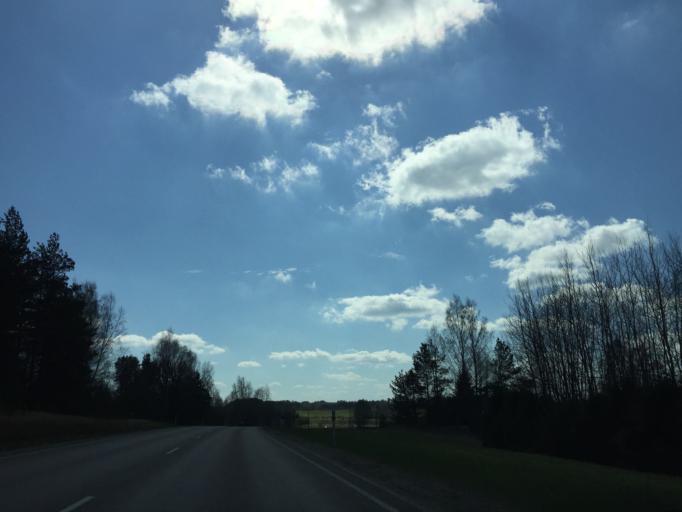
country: EE
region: Tartu
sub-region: Elva linn
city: Elva
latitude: 58.0925
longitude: 26.2255
